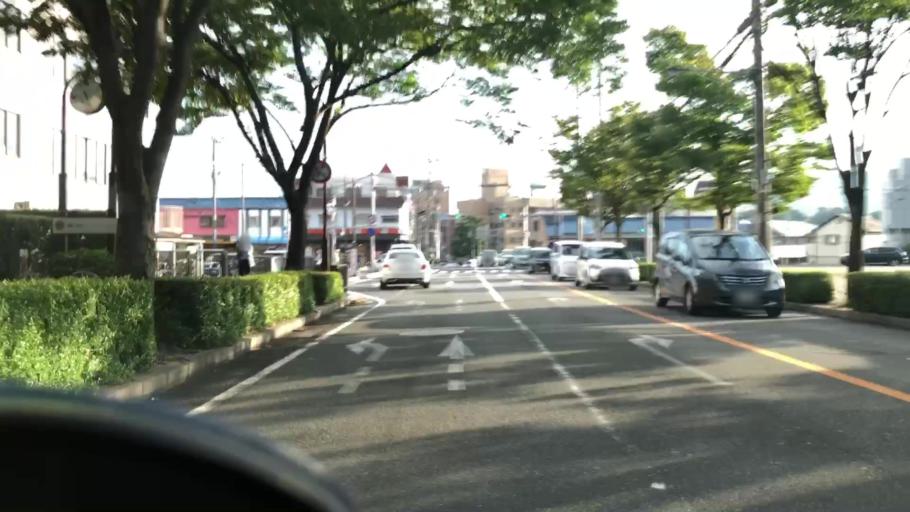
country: JP
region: Hyogo
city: Takarazuka
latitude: 34.7996
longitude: 135.3595
